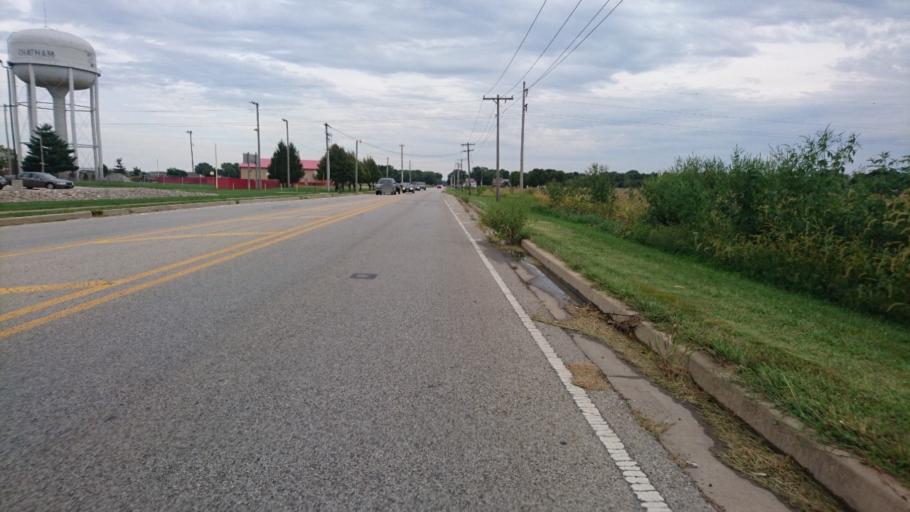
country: US
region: Illinois
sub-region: Sangamon County
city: Chatham
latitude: 39.6767
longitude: -89.6941
